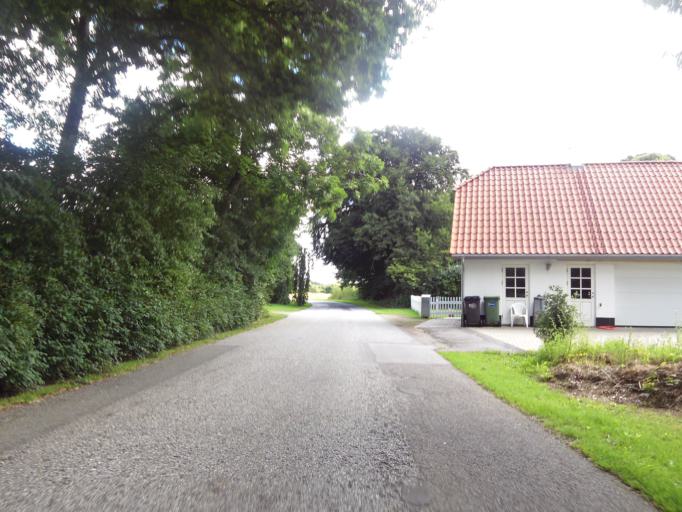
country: DK
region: South Denmark
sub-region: Haderslev Kommune
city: Vojens
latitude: 55.2804
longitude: 9.2255
